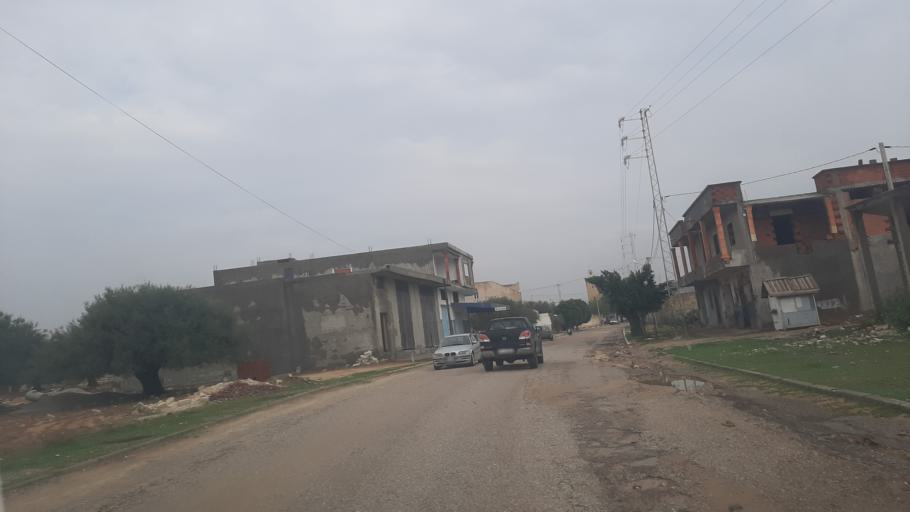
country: TN
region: Al Munastir
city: Sidi Bin Nur
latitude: 35.4783
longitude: 10.8738
